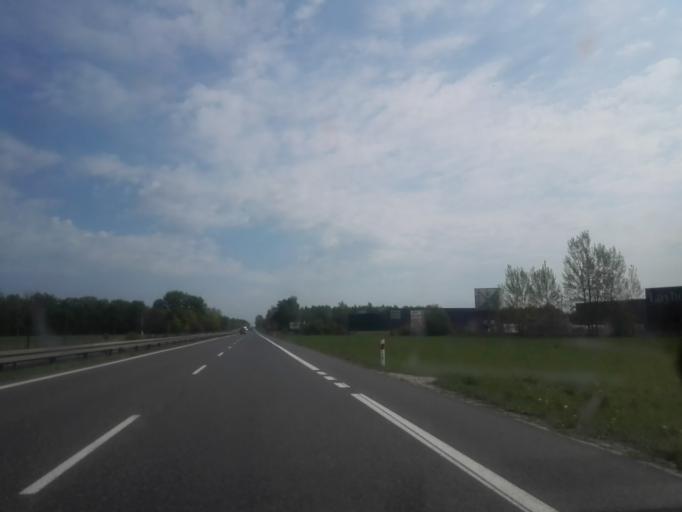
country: PL
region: Lodz Voivodeship
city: Zabia Wola
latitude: 52.0494
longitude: 20.7142
